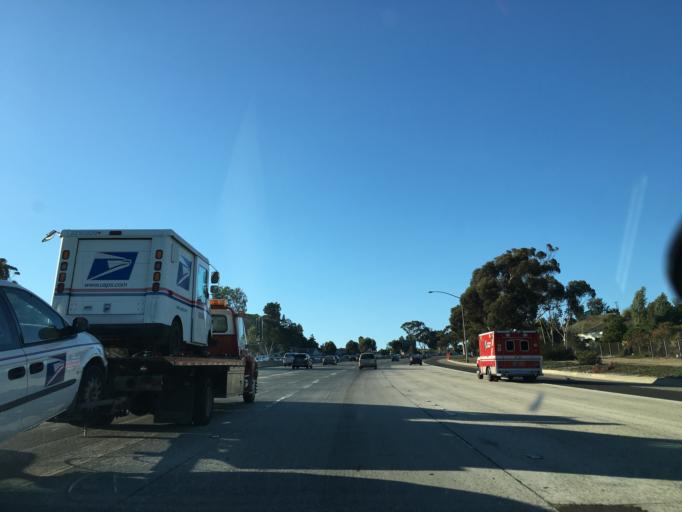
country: US
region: California
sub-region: San Diego County
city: San Diego
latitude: 32.7772
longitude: -117.1623
